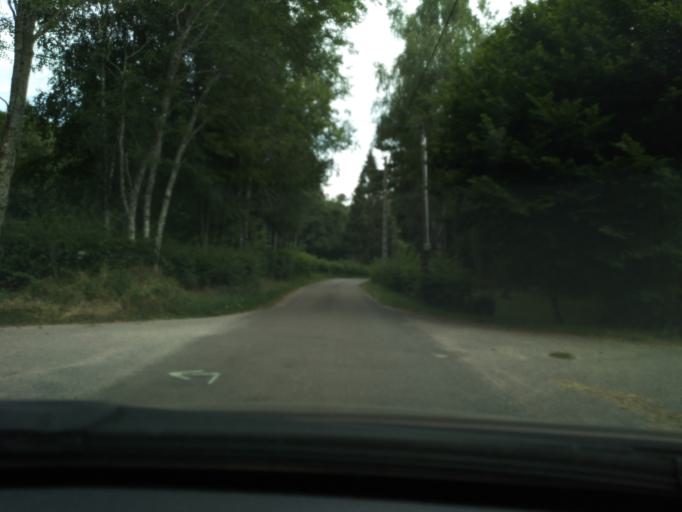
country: FR
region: Bourgogne
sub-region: Departement de la Cote-d'Or
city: Saulieu
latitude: 47.3485
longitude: 4.0926
